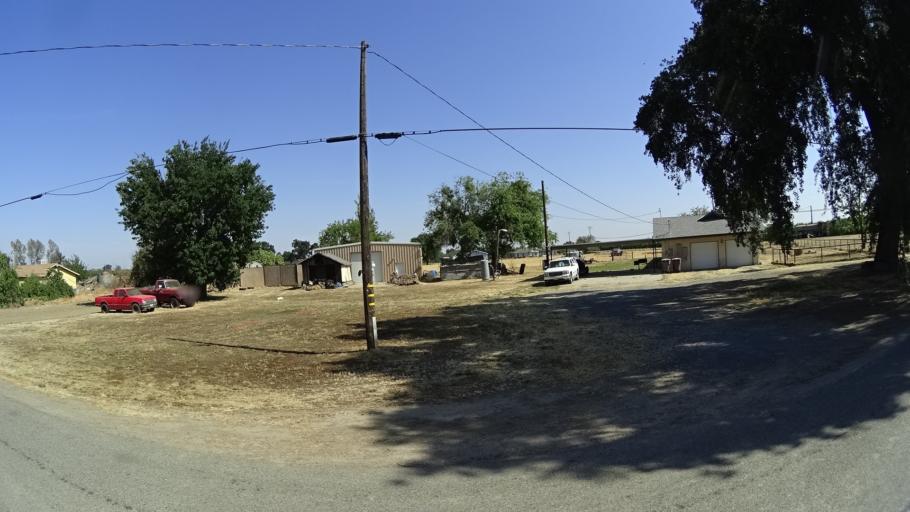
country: US
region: California
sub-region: Fresno County
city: Riverdale
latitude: 36.3512
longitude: -119.8522
